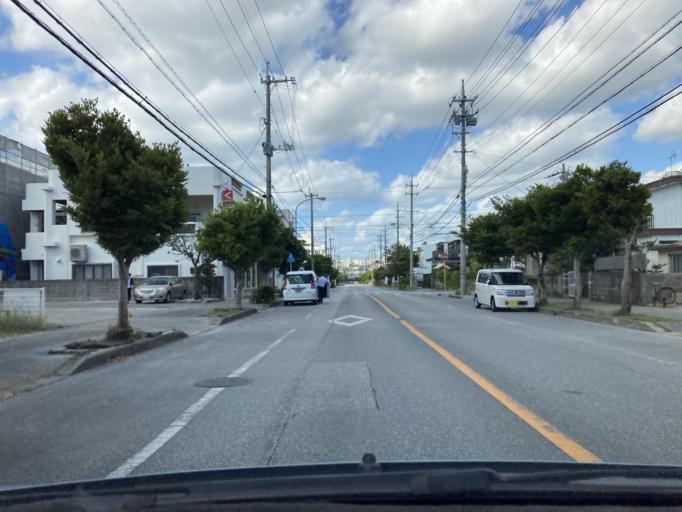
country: JP
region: Okinawa
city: Okinawa
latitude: 26.3198
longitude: 127.8365
